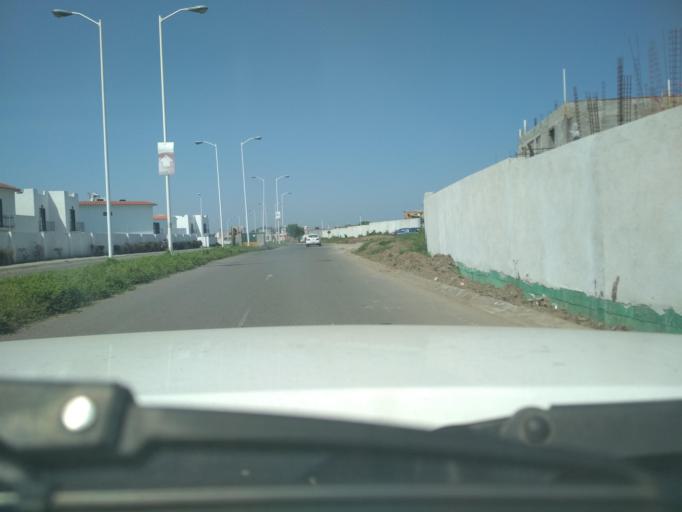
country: MX
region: Veracruz
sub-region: Veracruz
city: Lomas de Rio Medio Cuatro
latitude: 19.1790
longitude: -96.1902
